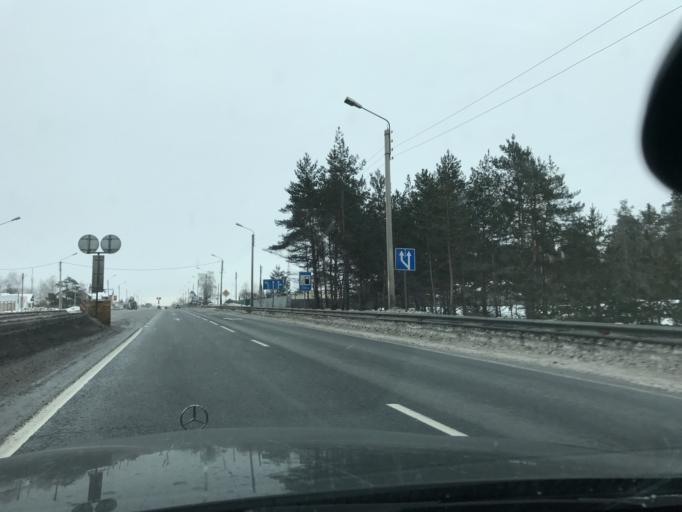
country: RU
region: Nizjnij Novgorod
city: Pyra
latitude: 56.2923
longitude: 43.3306
